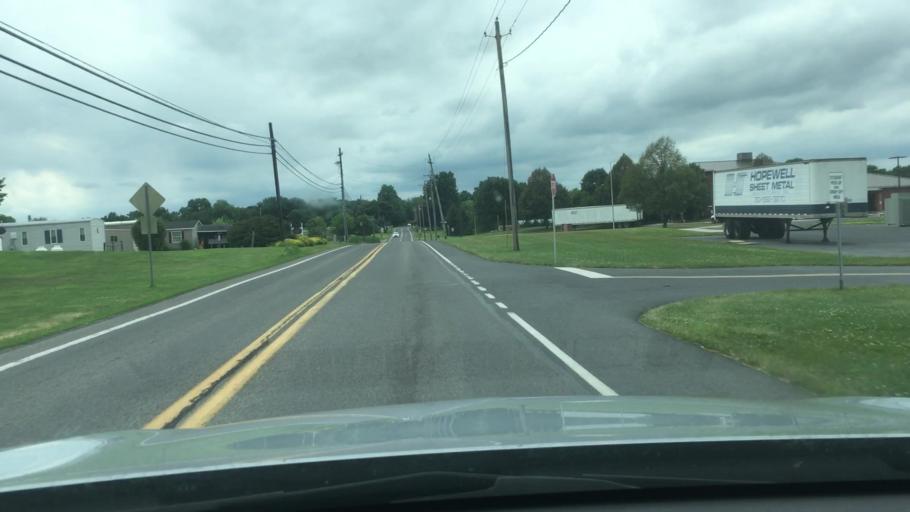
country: US
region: Pennsylvania
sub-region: Franklin County
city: Chambersburg
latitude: 39.9108
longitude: -77.7082
